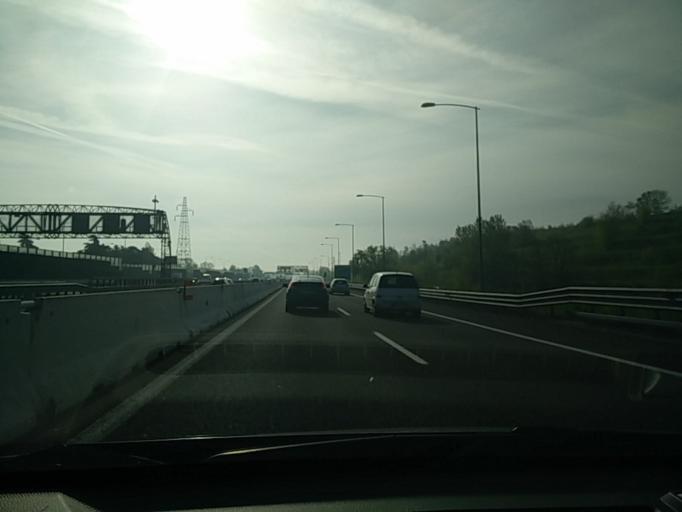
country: IT
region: Emilia-Romagna
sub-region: Provincia di Bologna
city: San Lazzaro
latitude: 44.4849
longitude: 11.4088
